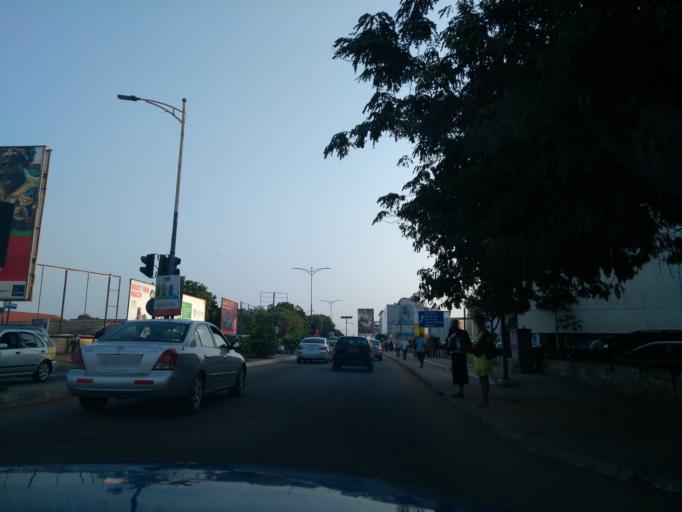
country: GH
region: Greater Accra
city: Accra
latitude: 5.5438
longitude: -0.2048
